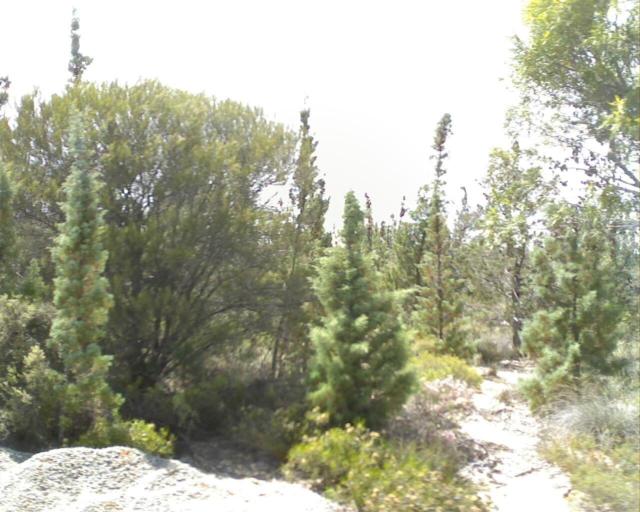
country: AU
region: Western Australia
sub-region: Moora
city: Moora
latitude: -30.0016
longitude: 115.8987
